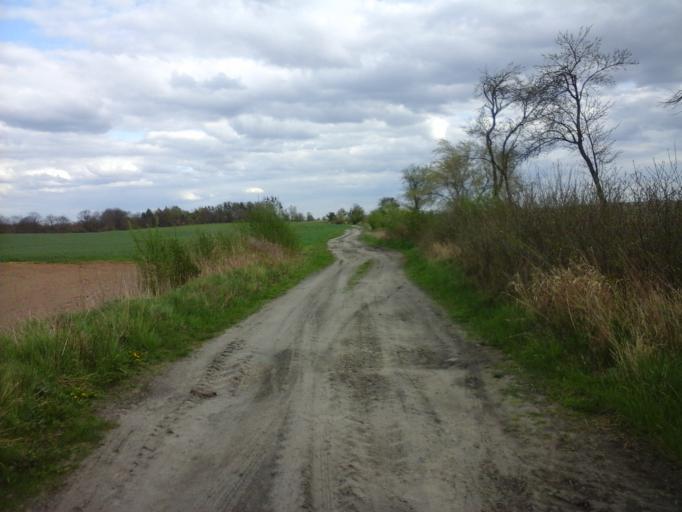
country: PL
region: West Pomeranian Voivodeship
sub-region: Powiat choszczenski
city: Krzecin
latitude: 53.1031
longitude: 15.5170
